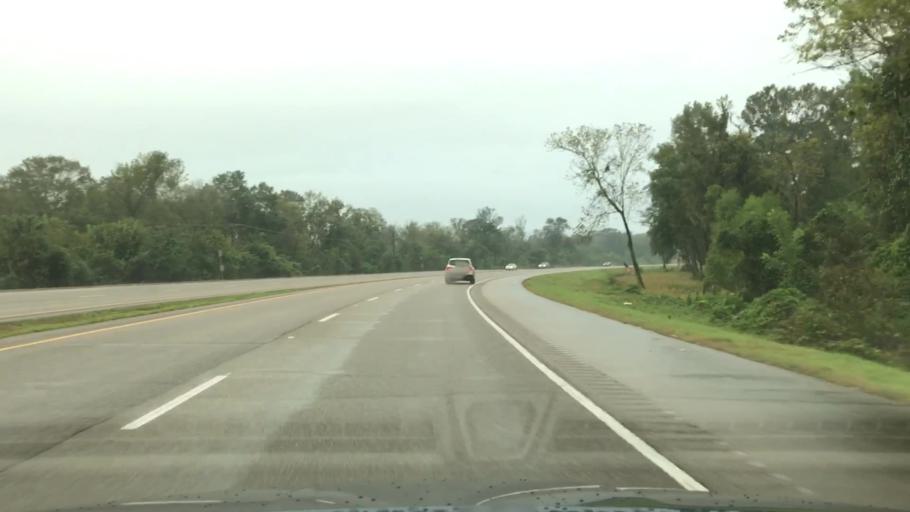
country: US
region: Louisiana
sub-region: Saint Charles Parish
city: Des Allemands
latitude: 29.8445
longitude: -90.4480
